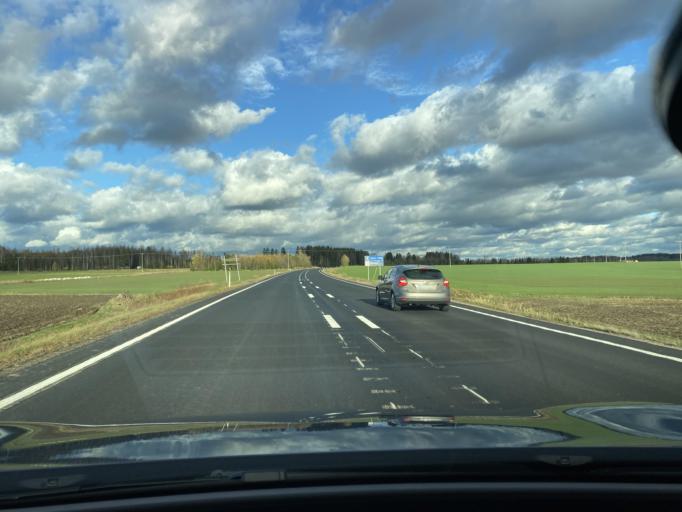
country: FI
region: Haeme
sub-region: Riihimaeki
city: Oitti
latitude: 60.8318
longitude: 25.0832
